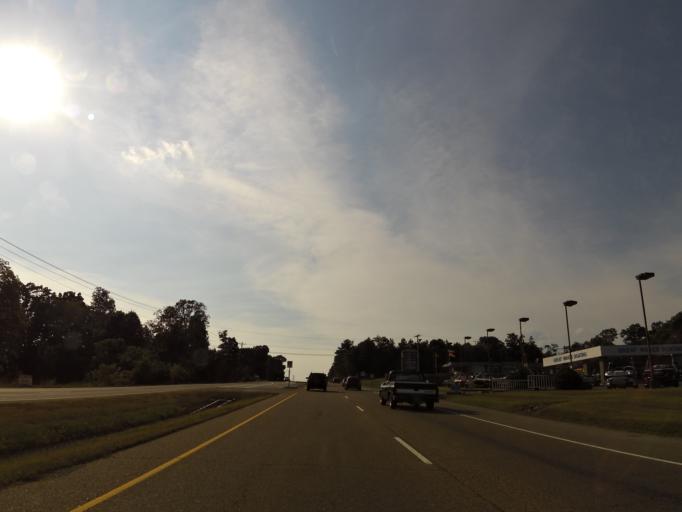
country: US
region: Tennessee
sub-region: Loudon County
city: Lenoir City
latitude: 35.8304
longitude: -84.2824
